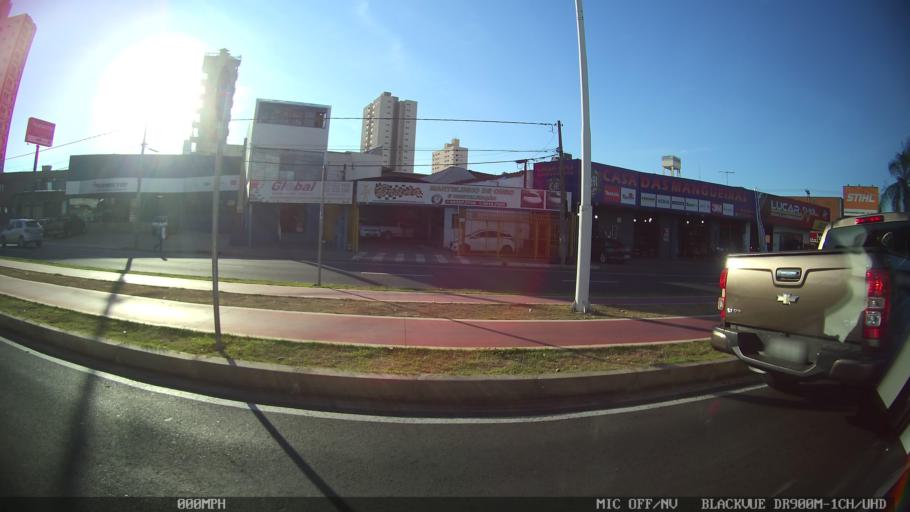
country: BR
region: Sao Paulo
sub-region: Sao Jose Do Rio Preto
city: Sao Jose do Rio Preto
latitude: -20.8080
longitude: -49.3809
